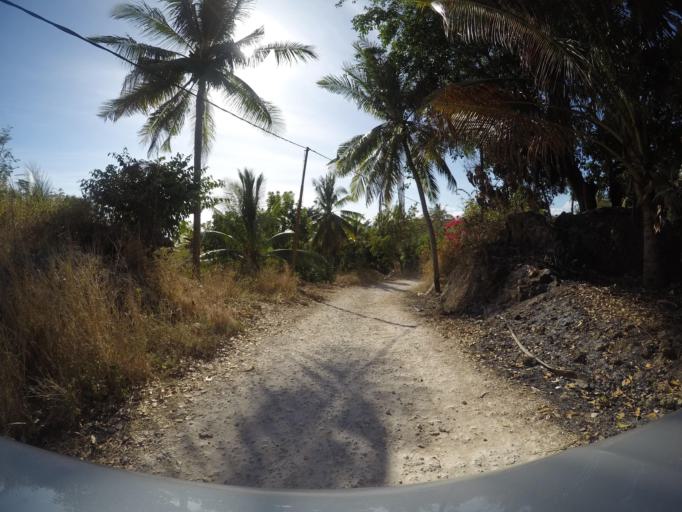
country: TL
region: Baucau
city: Baucau
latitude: -8.4509
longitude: 126.4328
